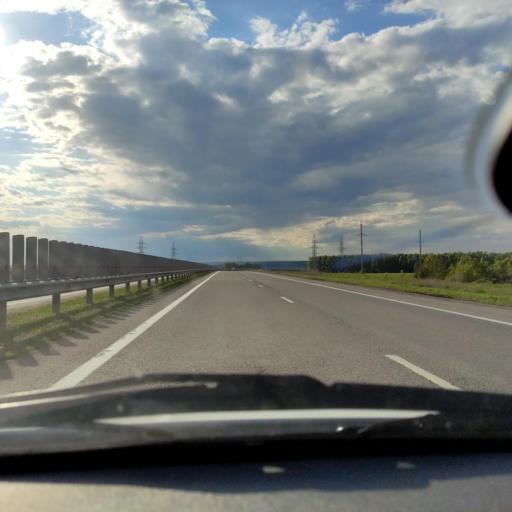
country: RU
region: Bashkortostan
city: Kushnarenkovo
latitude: 55.1324
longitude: 55.1836
